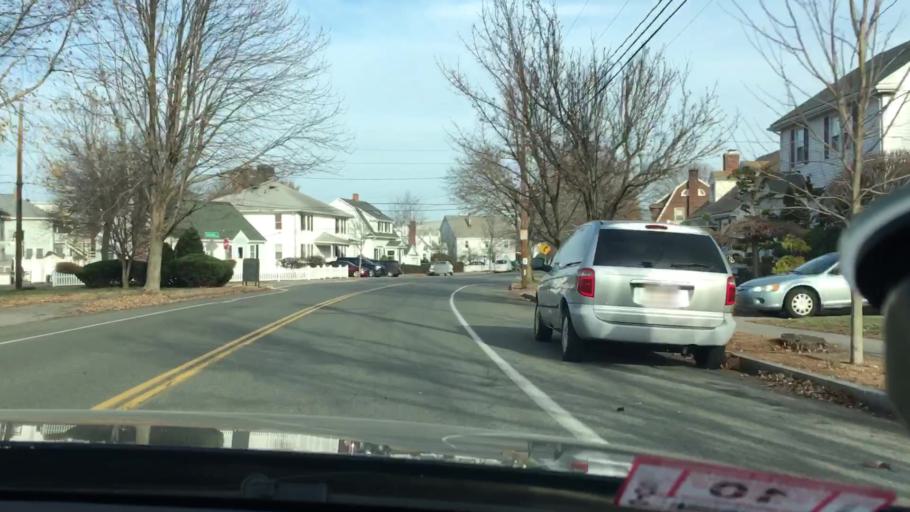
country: US
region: Massachusetts
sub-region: Norfolk County
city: Braintree
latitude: 42.2329
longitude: -71.0023
